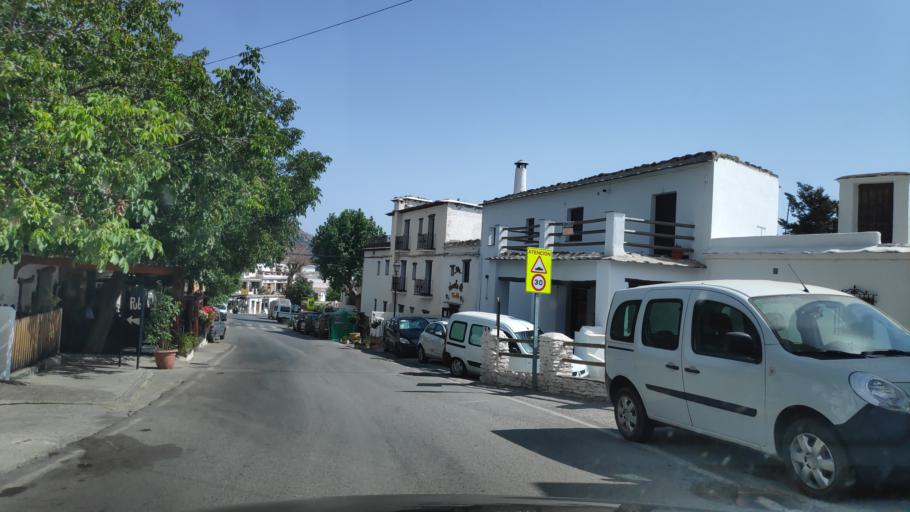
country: ES
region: Andalusia
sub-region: Provincia de Granada
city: Capileira
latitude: 36.9619
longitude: -3.3589
